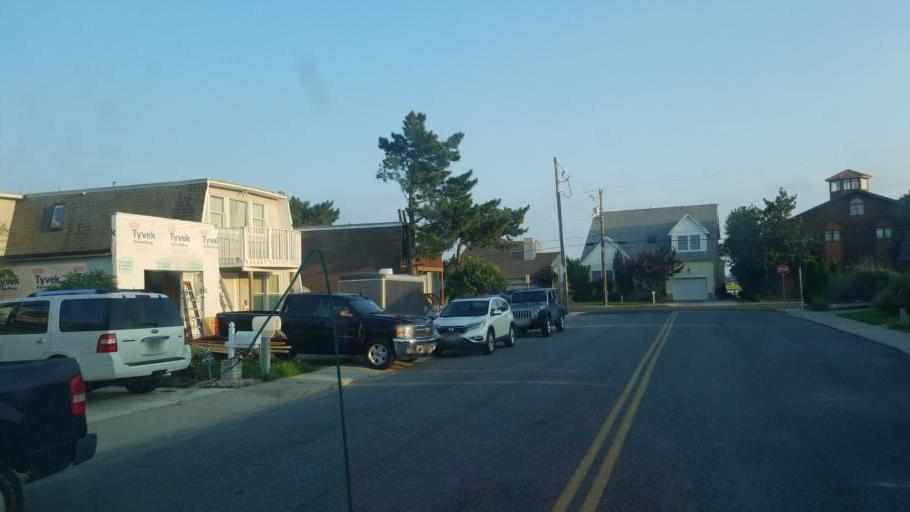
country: US
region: Maryland
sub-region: Worcester County
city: Ocean City
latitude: 38.4172
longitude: -75.0652
